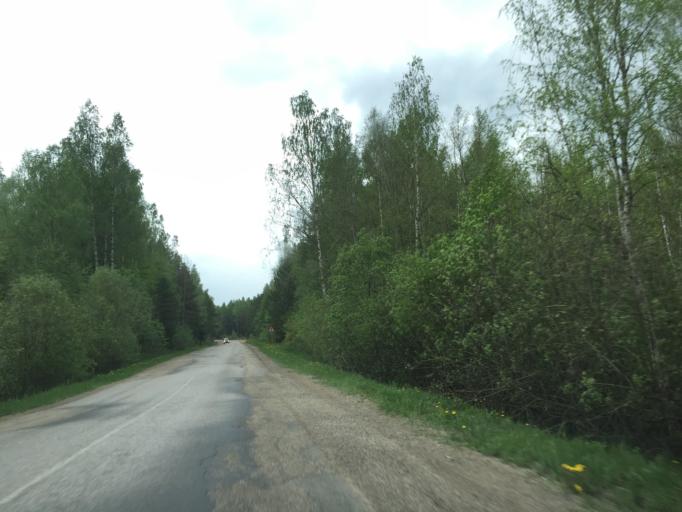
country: LV
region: Ogre
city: Ogre
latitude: 56.8395
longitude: 24.5766
